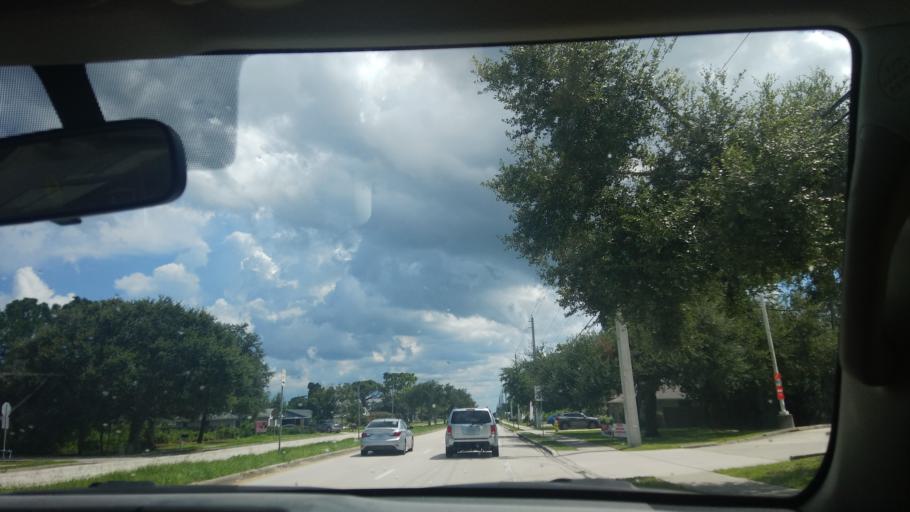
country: US
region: Florida
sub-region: Brevard County
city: Palm Bay
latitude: 27.9870
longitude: -80.6486
